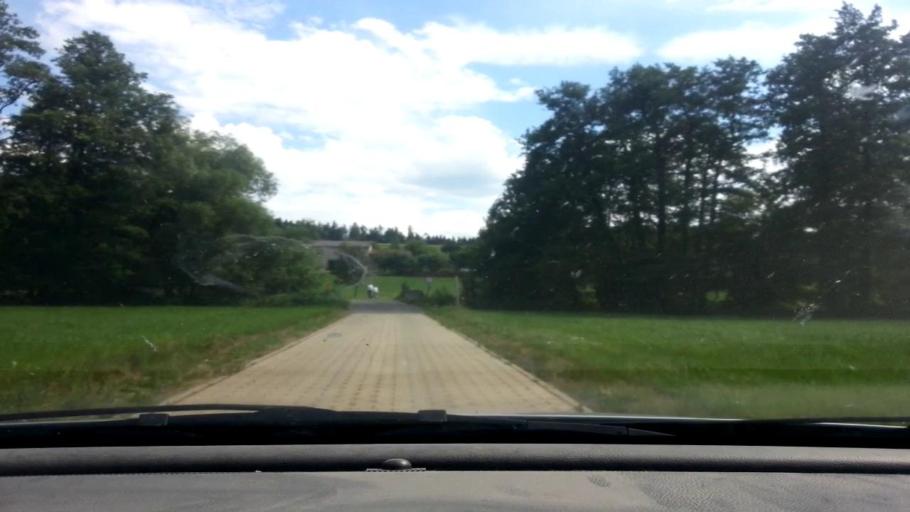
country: DE
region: Bavaria
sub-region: Upper Palatinate
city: Krummennaab
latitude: 49.8332
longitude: 12.0759
